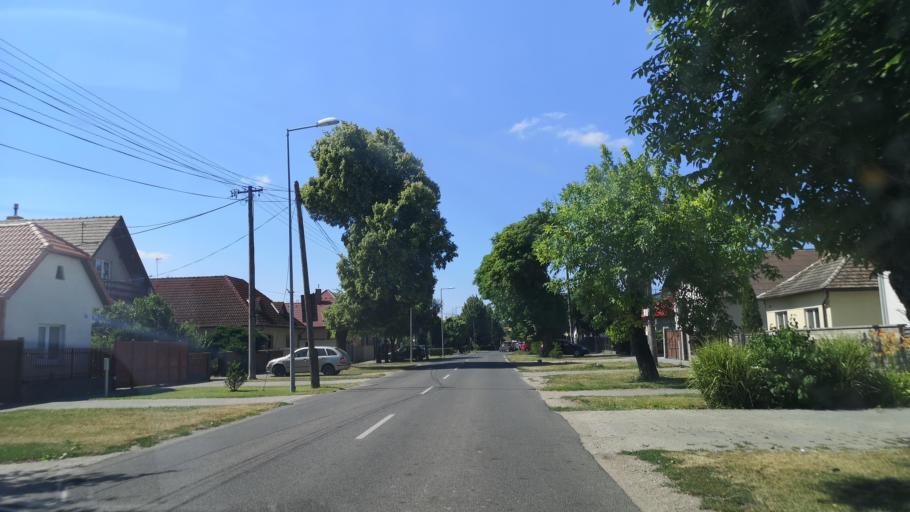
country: SK
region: Trnavsky
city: Samorin
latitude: 48.0521
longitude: 17.4591
